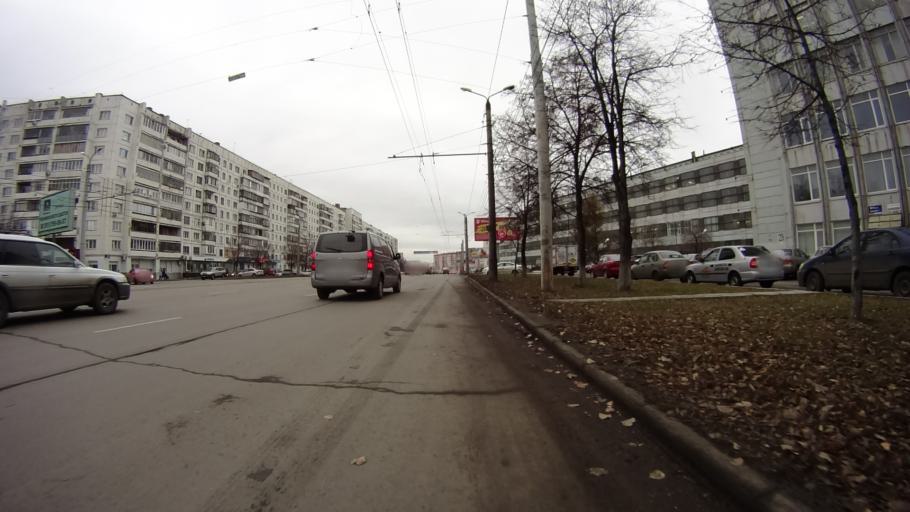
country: RU
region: Chelyabinsk
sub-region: Gorod Chelyabinsk
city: Chelyabinsk
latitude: 55.1937
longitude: 61.3560
